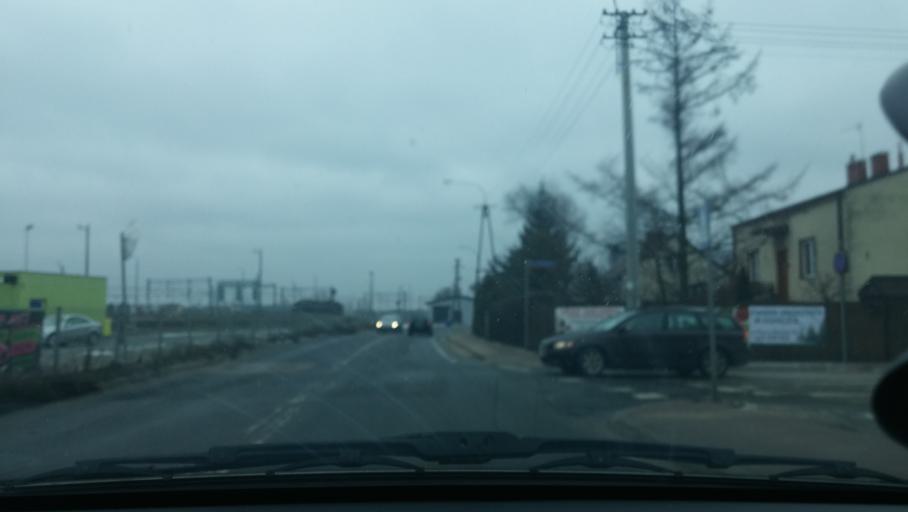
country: PL
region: Masovian Voivodeship
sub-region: Siedlce
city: Siedlce
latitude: 52.1584
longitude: 22.2758
